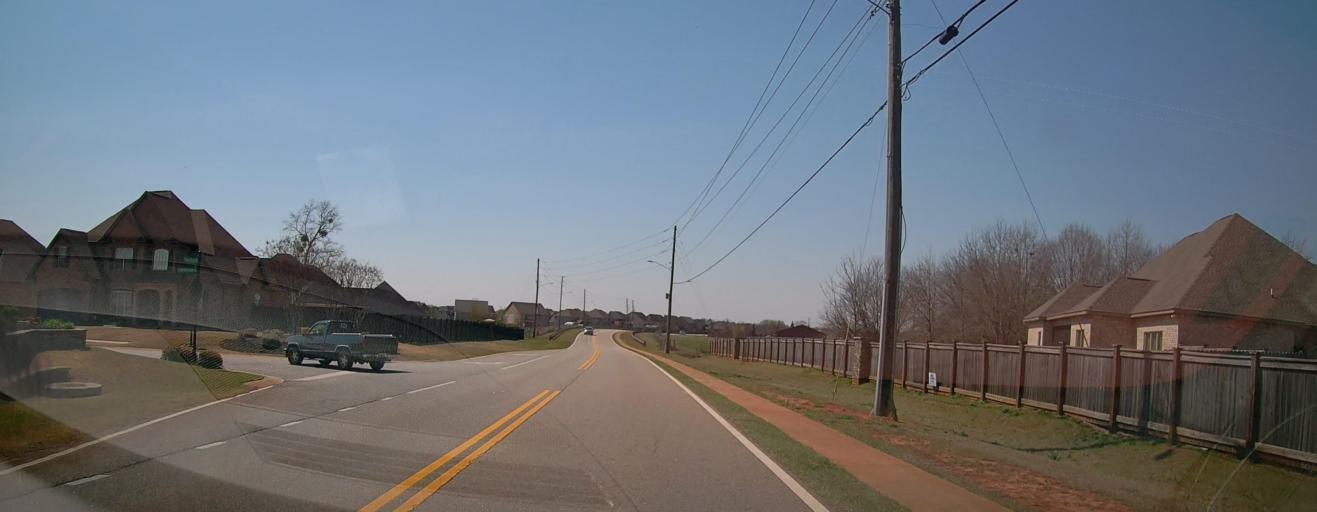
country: US
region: Georgia
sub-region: Houston County
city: Centerville
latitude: 32.5687
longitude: -83.7084
